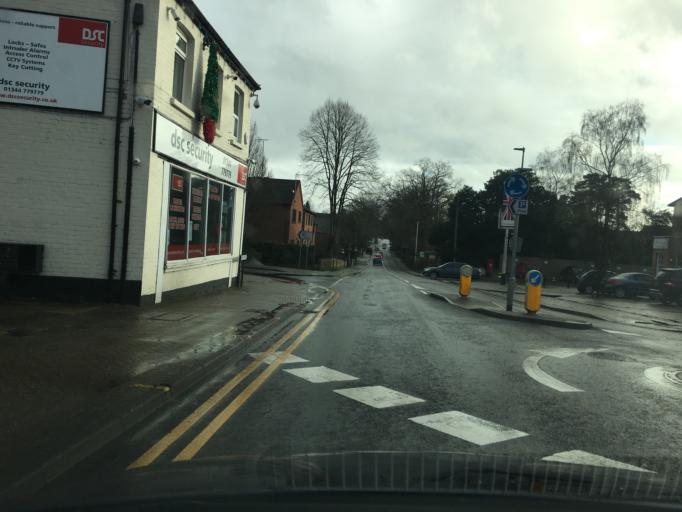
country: GB
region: England
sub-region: Bracknell Forest
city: Crowthorne
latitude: 51.3667
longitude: -0.7947
